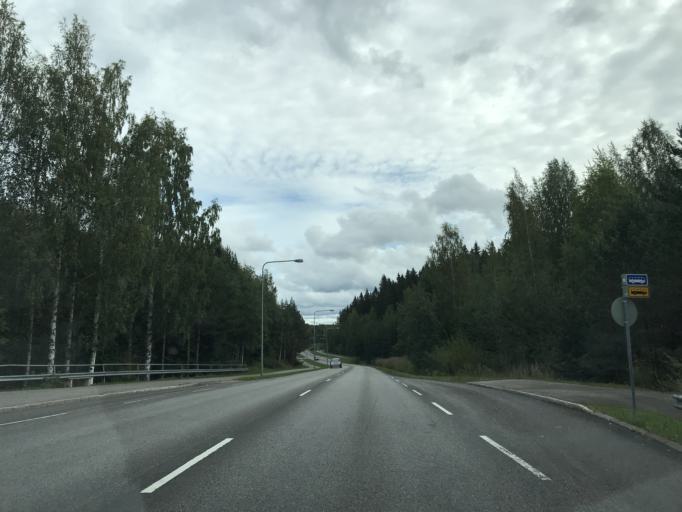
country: FI
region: Paijanne Tavastia
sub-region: Lahti
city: Lahti
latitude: 61.0020
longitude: 25.7664
